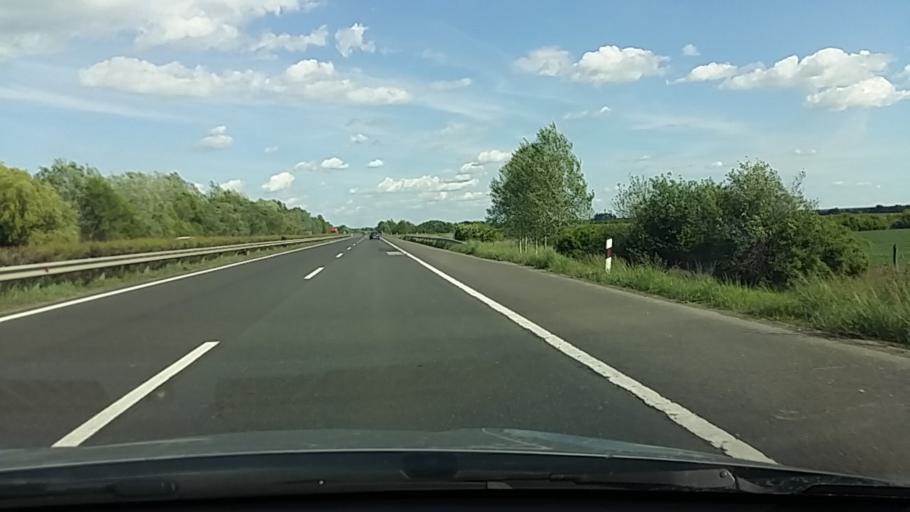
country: HU
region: Borsod-Abauj-Zemplen
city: Hejobaba
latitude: 47.8683
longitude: 20.9766
